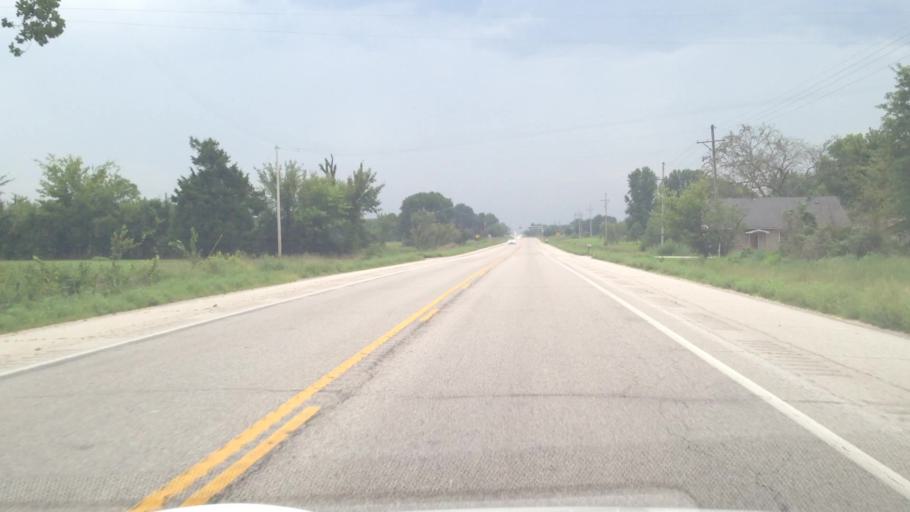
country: US
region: Kansas
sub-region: Cherokee County
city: Galena
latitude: 37.1180
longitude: -94.7044
